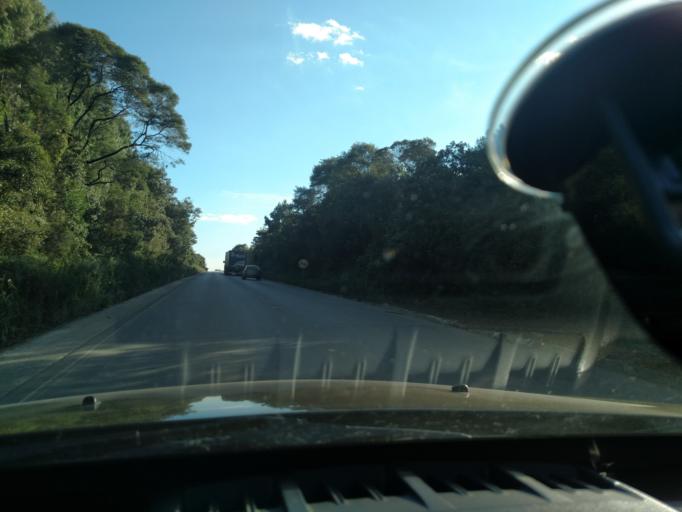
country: BR
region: Santa Catarina
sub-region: Otacilio Costa
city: Otacilio Costa
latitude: -27.5276
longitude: -50.1389
